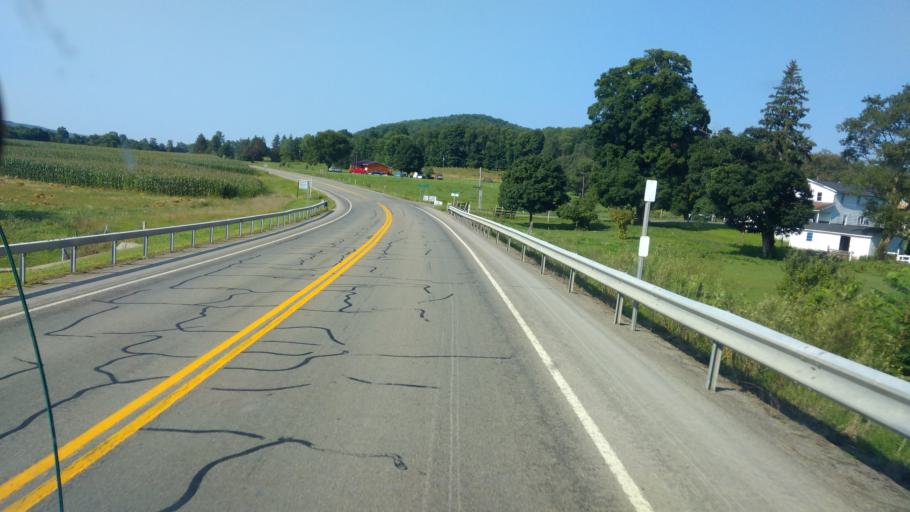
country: US
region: New York
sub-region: Allegany County
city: Friendship
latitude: 42.3005
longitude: -78.1877
